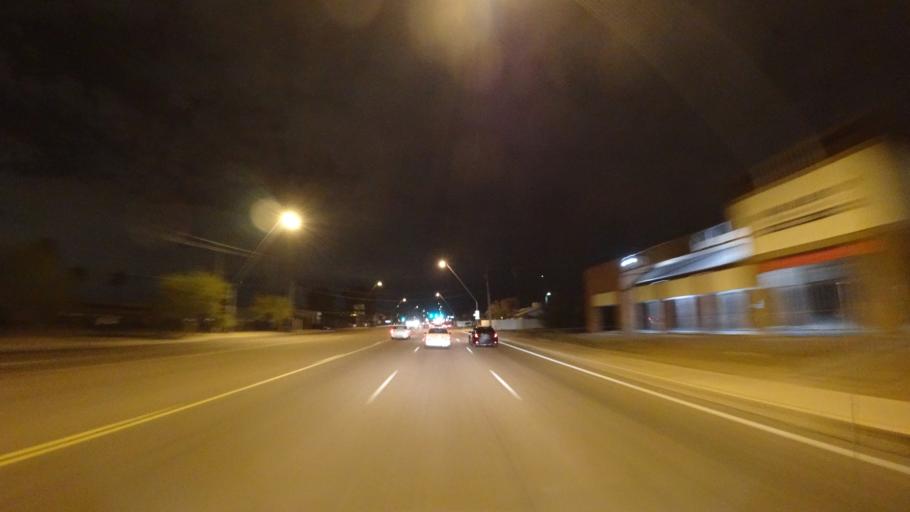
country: US
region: Arizona
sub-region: Maricopa County
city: Mesa
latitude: 33.3944
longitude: -111.8571
